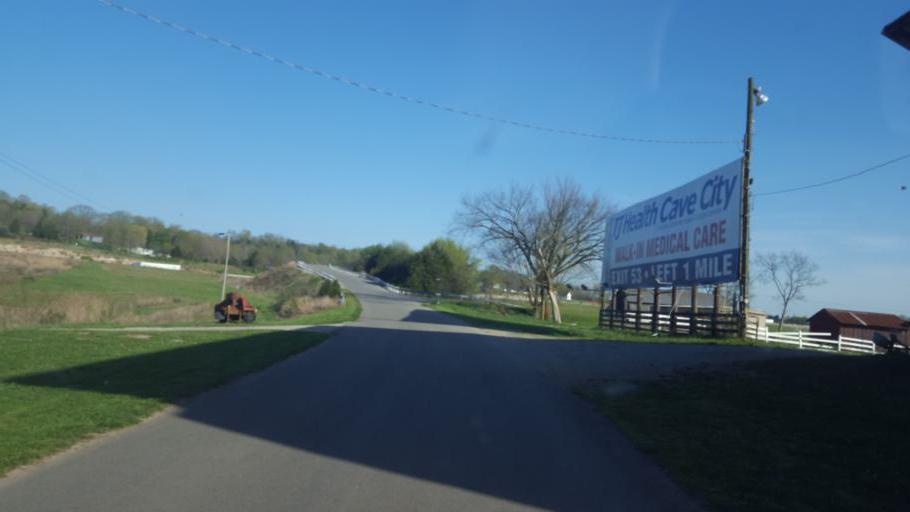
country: US
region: Kentucky
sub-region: Barren County
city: Cave City
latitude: 37.1585
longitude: -85.9737
